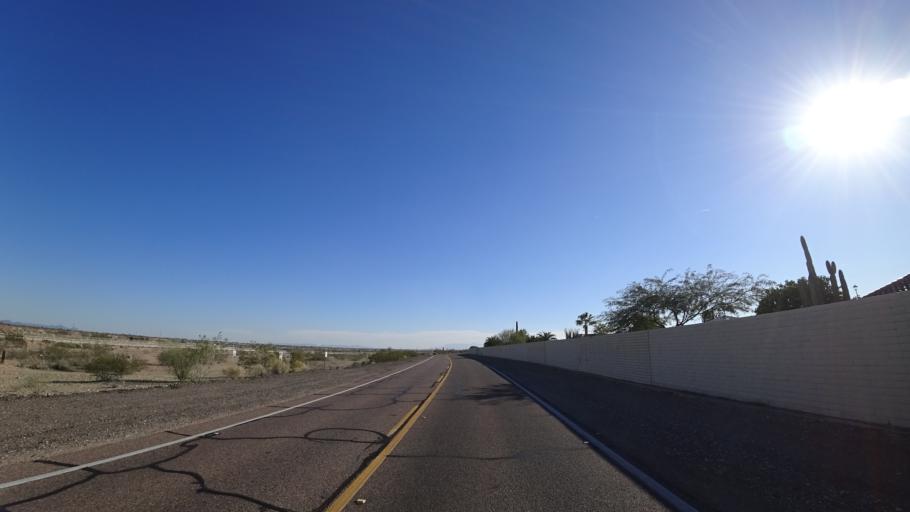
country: US
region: Arizona
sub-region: Maricopa County
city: Sun City West
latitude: 33.6637
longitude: -112.3255
